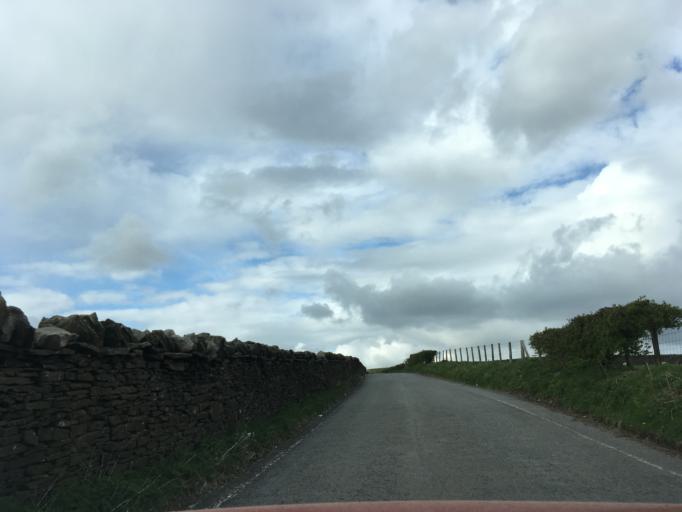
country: GB
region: Wales
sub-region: Merthyr Tydfil County Borough
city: Treharris
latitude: 51.7100
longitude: -3.3101
